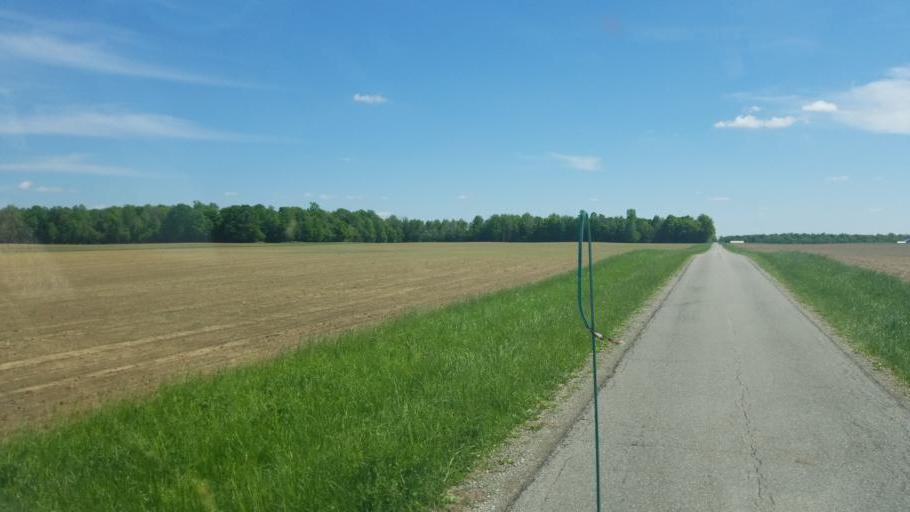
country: US
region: Ohio
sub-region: Crawford County
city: Bucyrus
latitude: 40.9483
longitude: -83.0356
